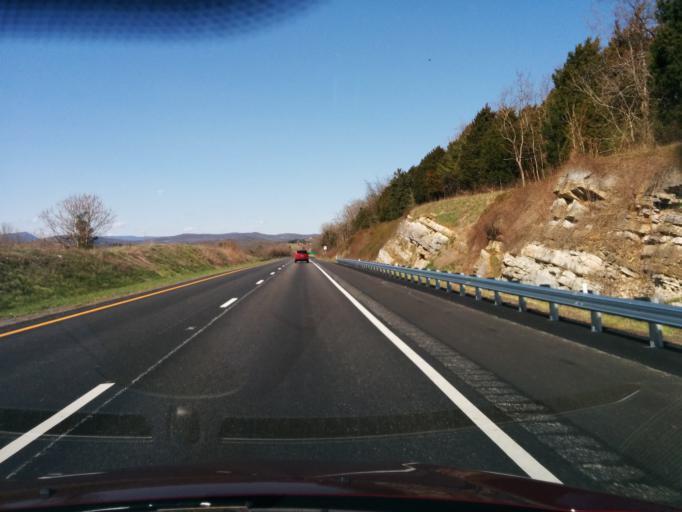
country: US
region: Virginia
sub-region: Rockbridge County
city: East Lexington
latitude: 37.7644
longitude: -79.4058
